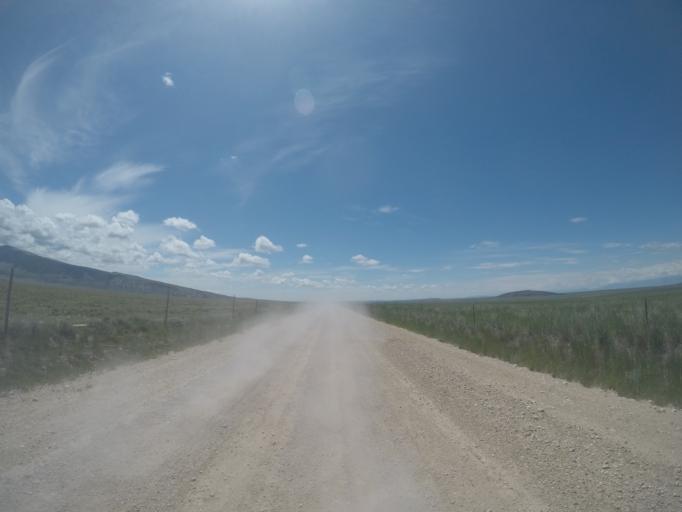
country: US
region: Montana
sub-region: Yellowstone County
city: Laurel
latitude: 45.2310
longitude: -108.6995
